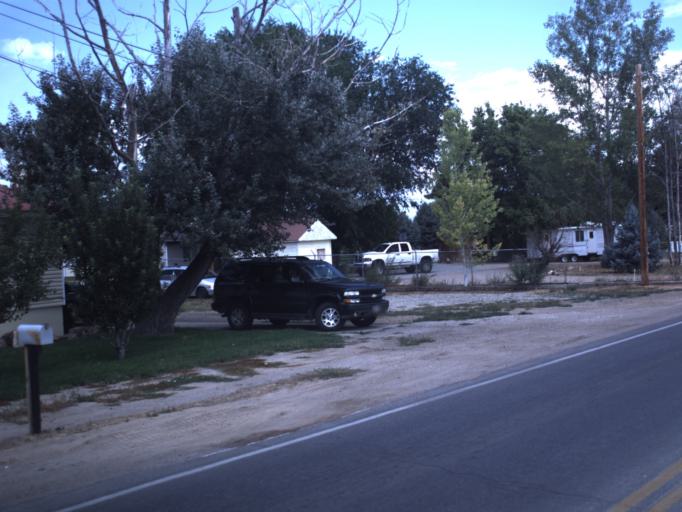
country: US
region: Utah
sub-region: Uintah County
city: Naples
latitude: 40.4060
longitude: -109.4990
